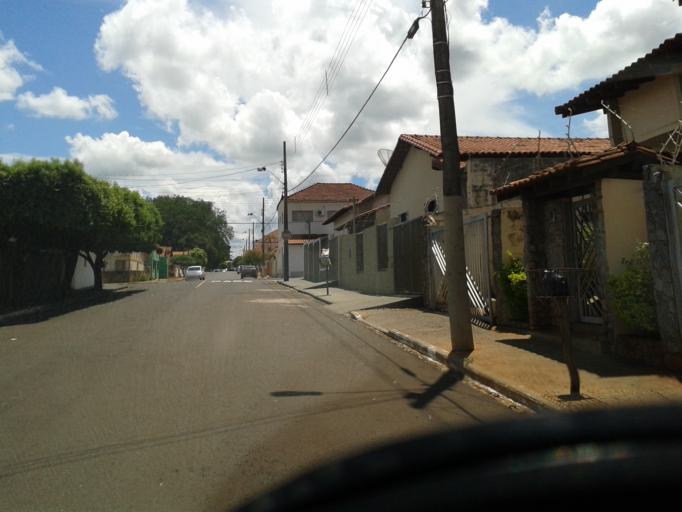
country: BR
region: Minas Gerais
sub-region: Ituiutaba
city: Ituiutaba
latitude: -18.9755
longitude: -49.4709
